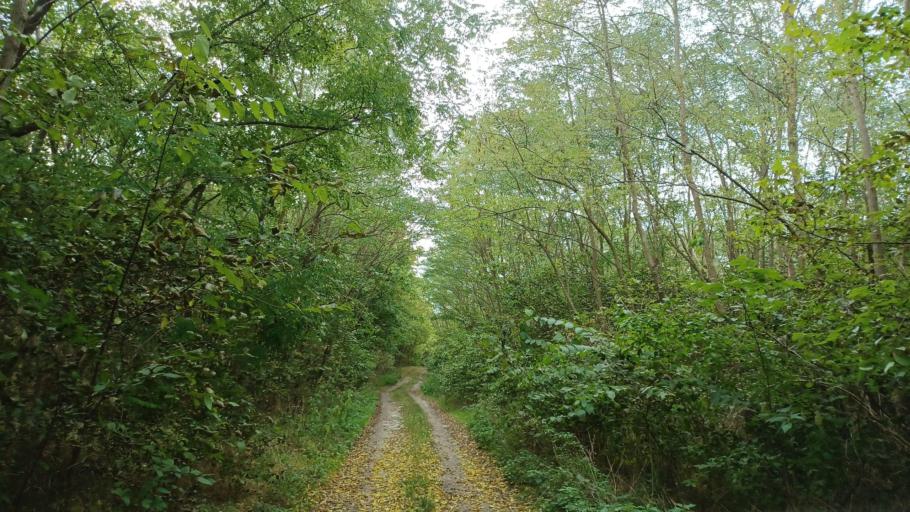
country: HU
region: Tolna
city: Tengelic
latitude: 46.5759
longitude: 18.7275
